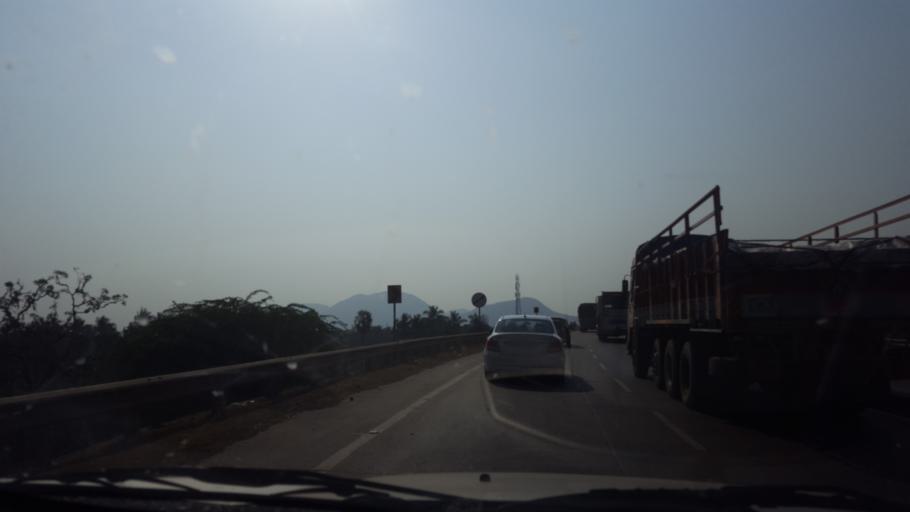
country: IN
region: Andhra Pradesh
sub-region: Vishakhapatnam
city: Anakapalle
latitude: 17.6506
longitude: 82.9223
